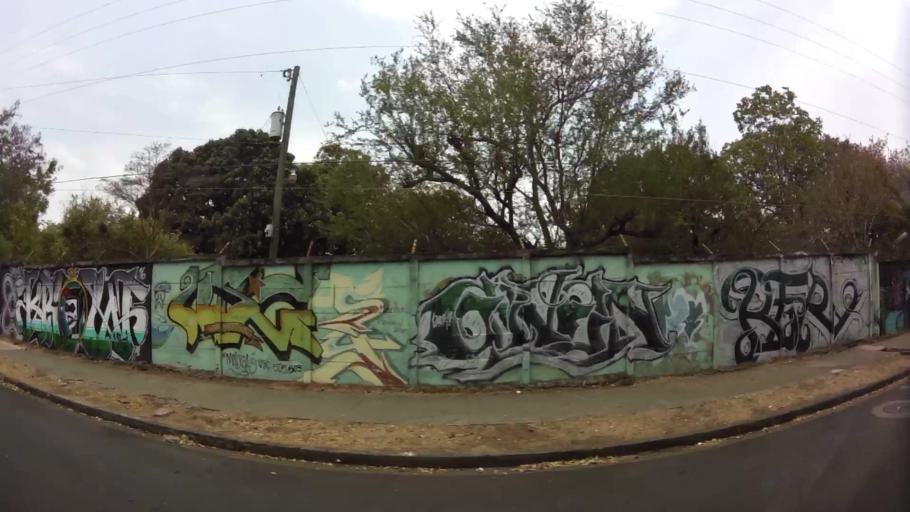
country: NI
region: Managua
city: Managua
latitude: 12.1305
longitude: -86.2951
